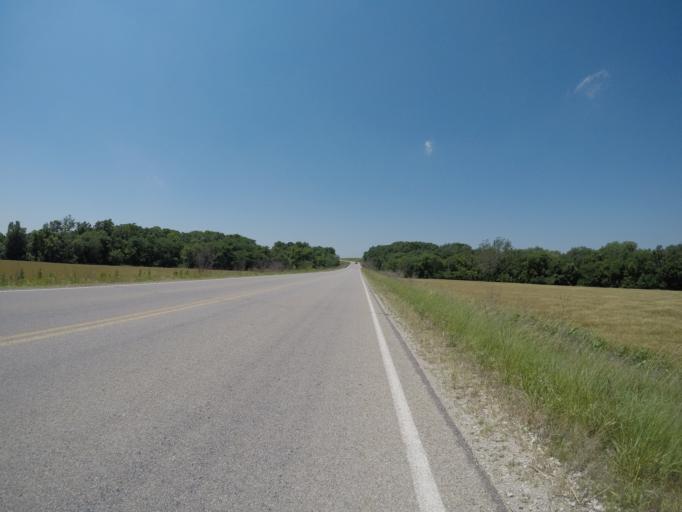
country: US
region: Kansas
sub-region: Pottawatomie County
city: Westmoreland
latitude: 39.2872
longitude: -96.4421
